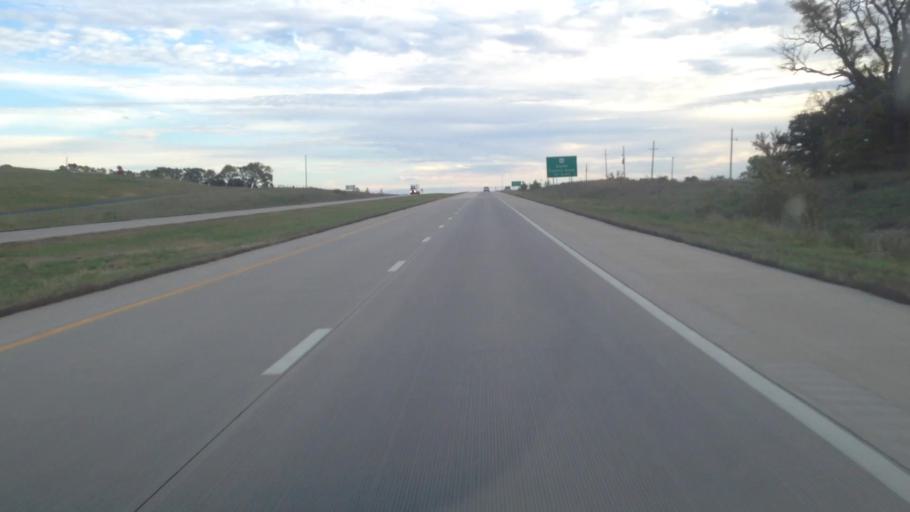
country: US
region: Kansas
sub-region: Douglas County
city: Baldwin City
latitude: 38.7971
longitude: -95.2692
